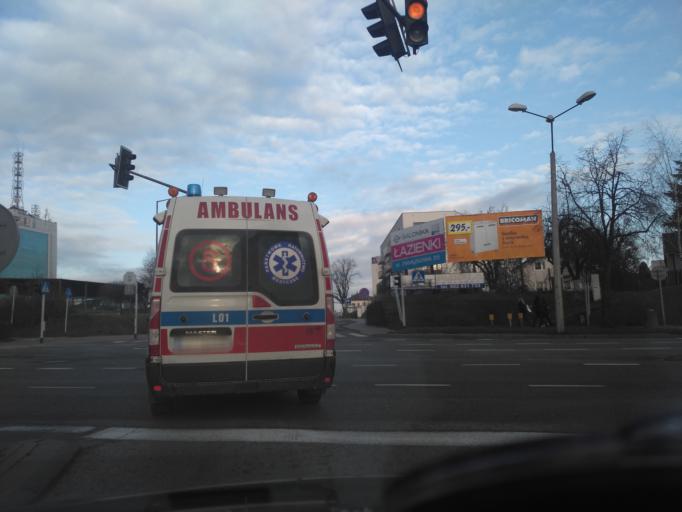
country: PL
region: Lublin Voivodeship
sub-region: Powiat lubelski
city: Lublin
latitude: 51.2633
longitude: 22.5629
